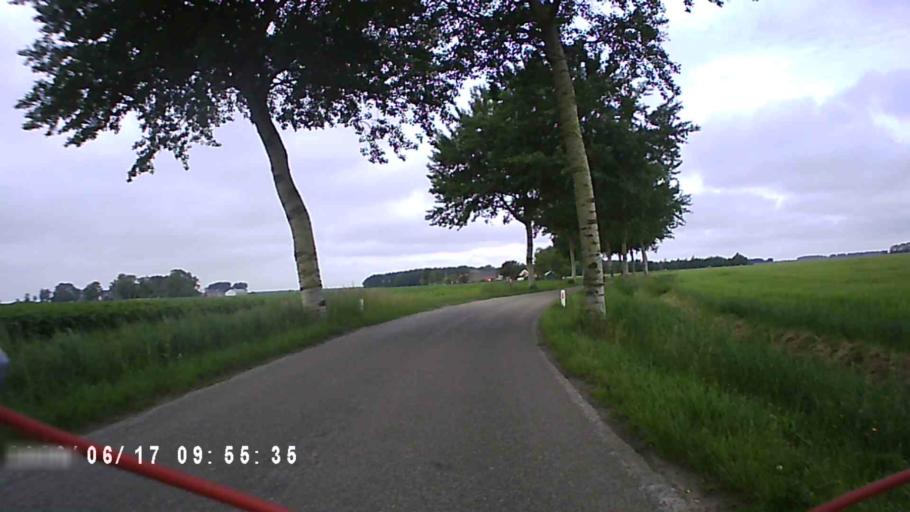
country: NL
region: Groningen
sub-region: Gemeente De Marne
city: Ulrum
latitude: 53.3596
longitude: 6.3047
